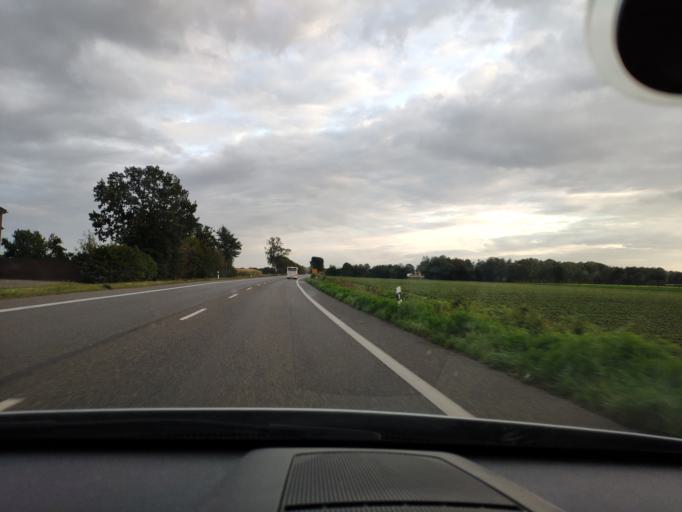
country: DE
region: North Rhine-Westphalia
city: Geilenkirchen
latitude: 51.0065
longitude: 6.1193
